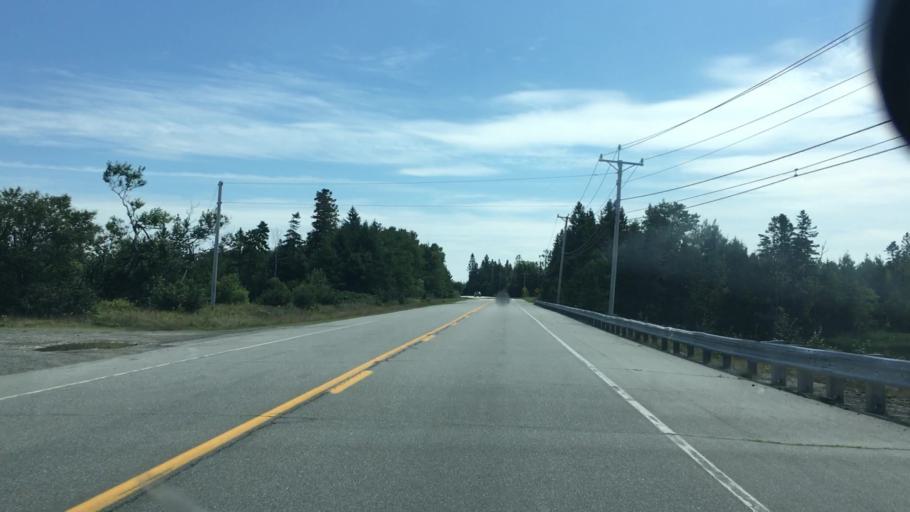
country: US
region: Maine
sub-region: Washington County
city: Eastport
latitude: 44.9459
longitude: -67.0393
